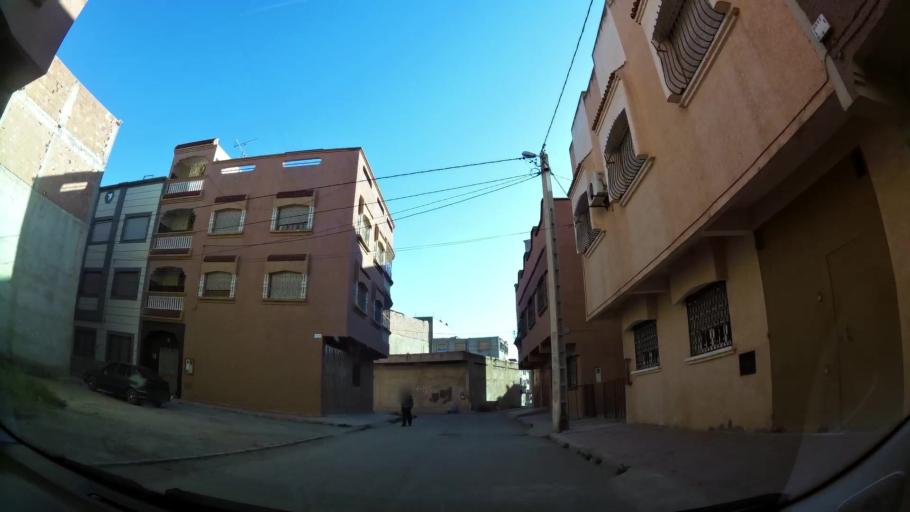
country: MA
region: Oriental
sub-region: Berkane-Taourirt
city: Berkane
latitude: 34.9275
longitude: -2.3395
